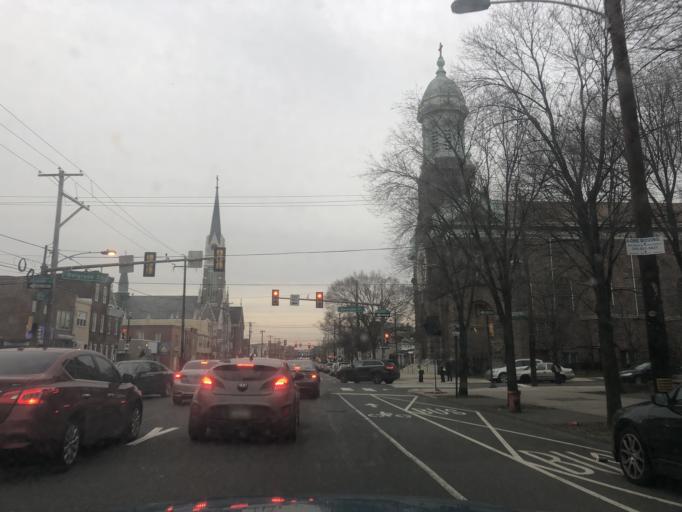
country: US
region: New Jersey
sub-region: Camden County
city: Merchantville
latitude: 39.9861
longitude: -75.1040
